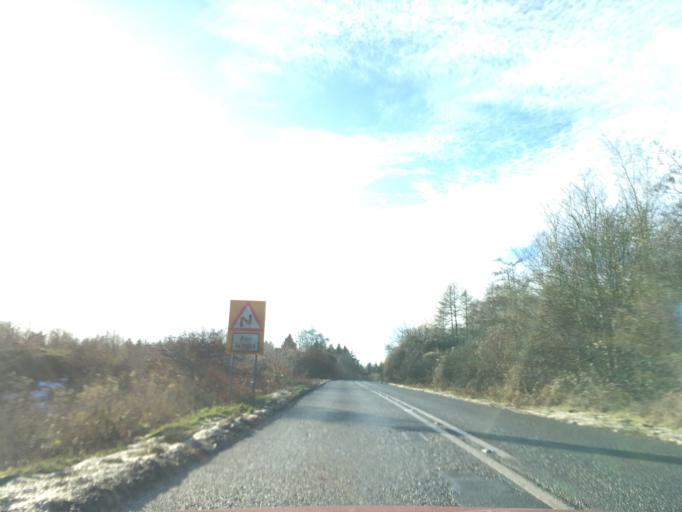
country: GB
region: England
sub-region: Gloucestershire
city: Mitcheldean
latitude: 51.8494
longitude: -2.4969
